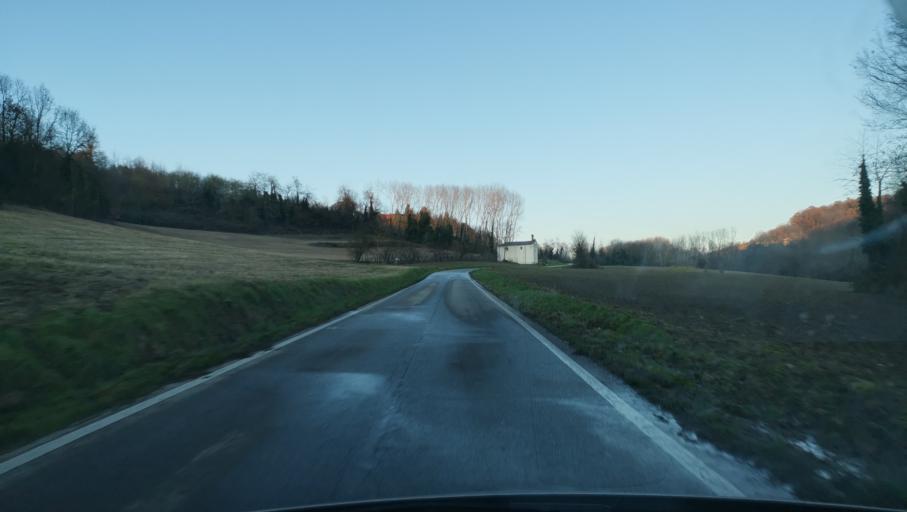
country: IT
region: Piedmont
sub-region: Provincia di Asti
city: Berzano di San Pietro
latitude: 45.0852
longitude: 7.9445
